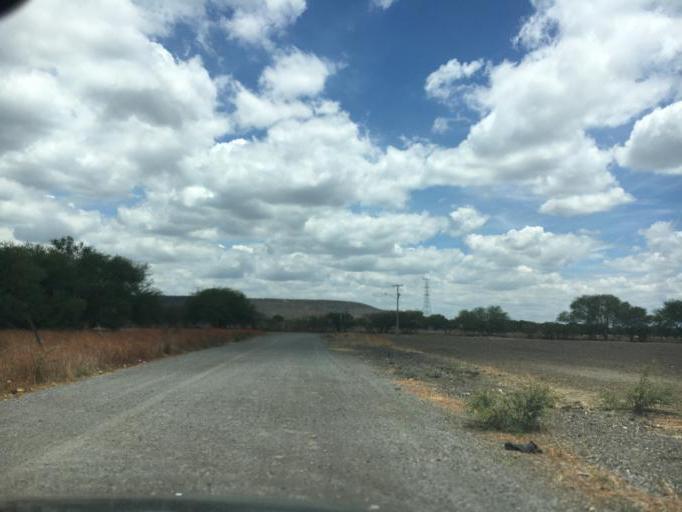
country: MX
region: Guanajuato
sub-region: Leon
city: Plan Guanajuato (La Sandia)
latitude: 20.9179
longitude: -101.7485
